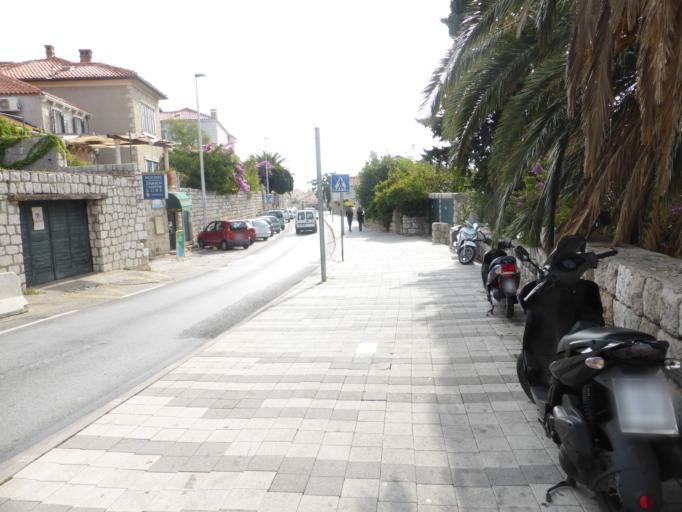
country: HR
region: Dubrovacko-Neretvanska
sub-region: Grad Dubrovnik
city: Dubrovnik
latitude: 42.6452
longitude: 18.1036
